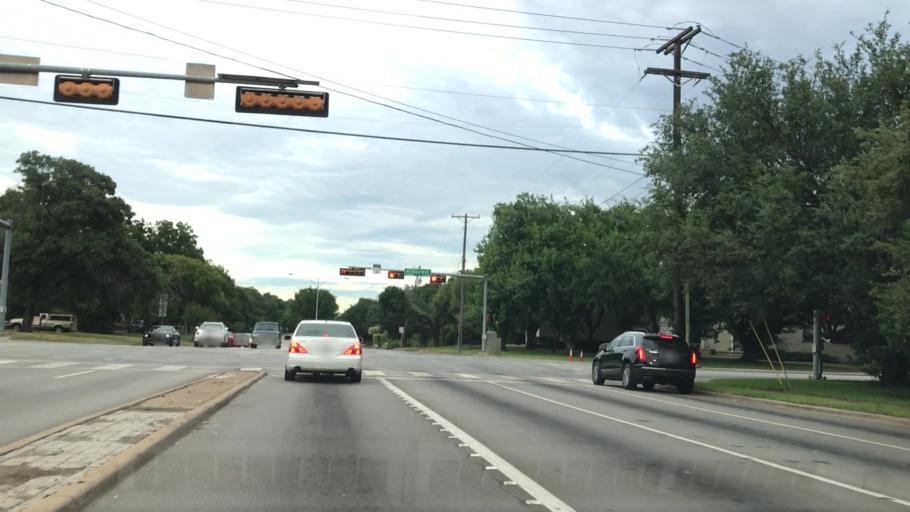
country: US
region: Texas
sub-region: Dallas County
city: University Park
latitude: 32.8948
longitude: -96.7882
